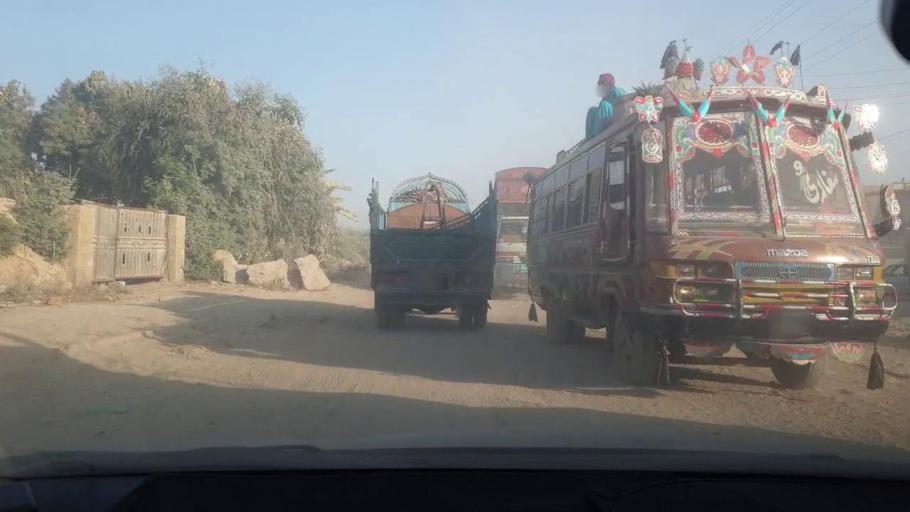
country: PK
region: Sindh
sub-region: Karachi District
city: Karachi
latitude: 24.9725
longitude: 67.0397
